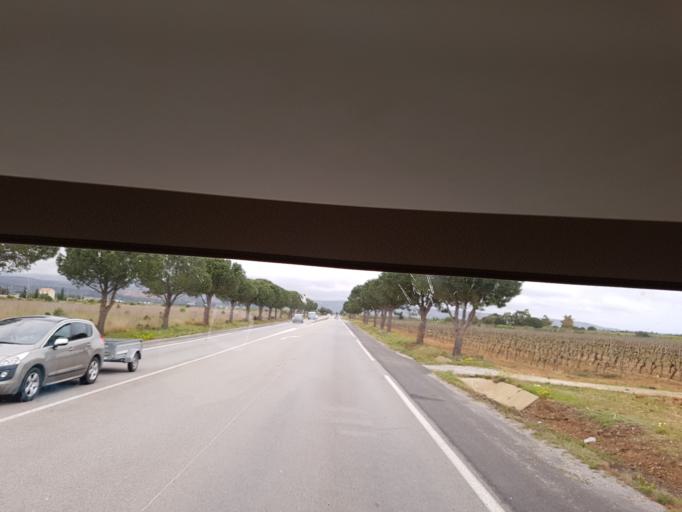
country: FR
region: Languedoc-Roussillon
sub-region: Departement des Pyrenees-Orientales
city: Salses-le-Chateau
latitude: 42.8060
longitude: 2.9118
